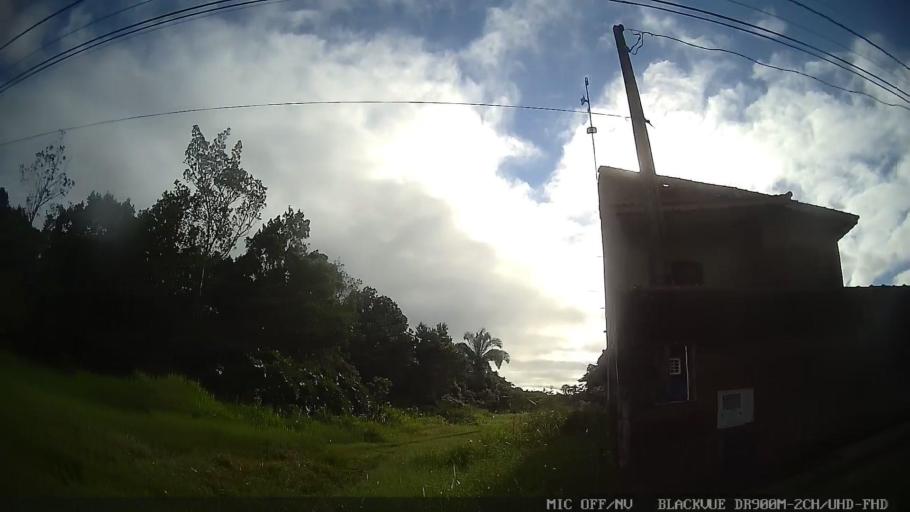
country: BR
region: Sao Paulo
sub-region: Peruibe
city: Peruibe
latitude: -24.2378
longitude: -46.9093
